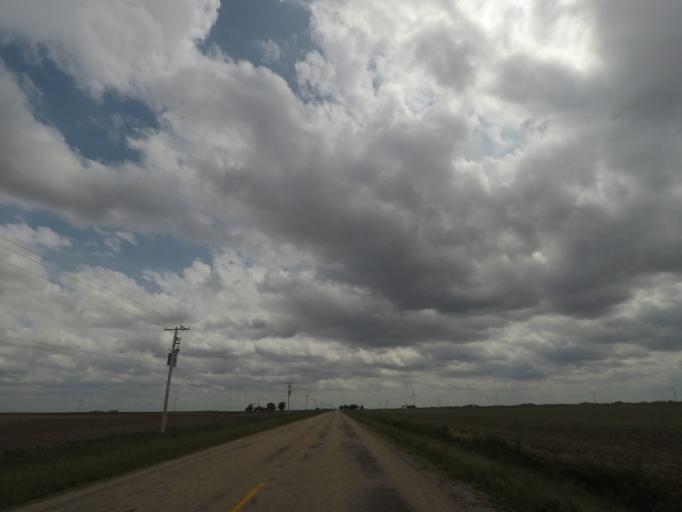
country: US
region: Illinois
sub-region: Macon County
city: Maroa
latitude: 40.0697
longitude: -89.0860
